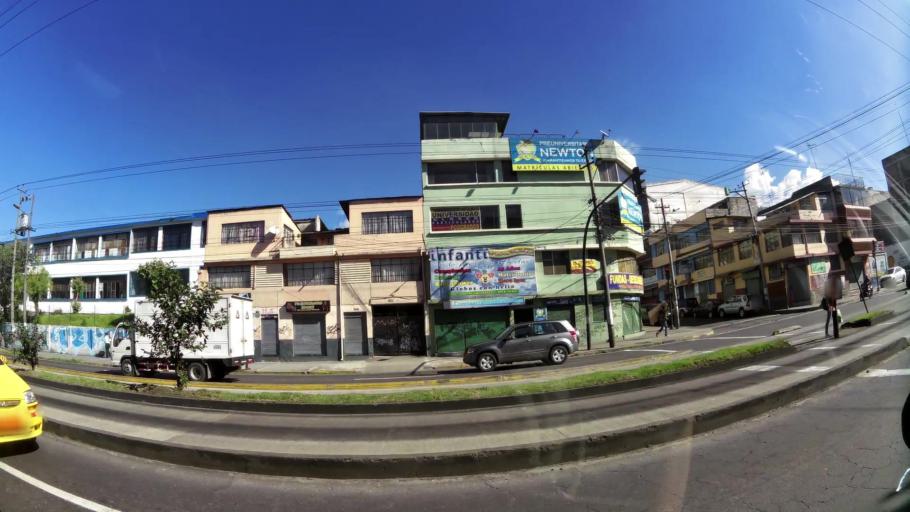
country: EC
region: Pichincha
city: Quito
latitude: -0.2397
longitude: -78.5308
